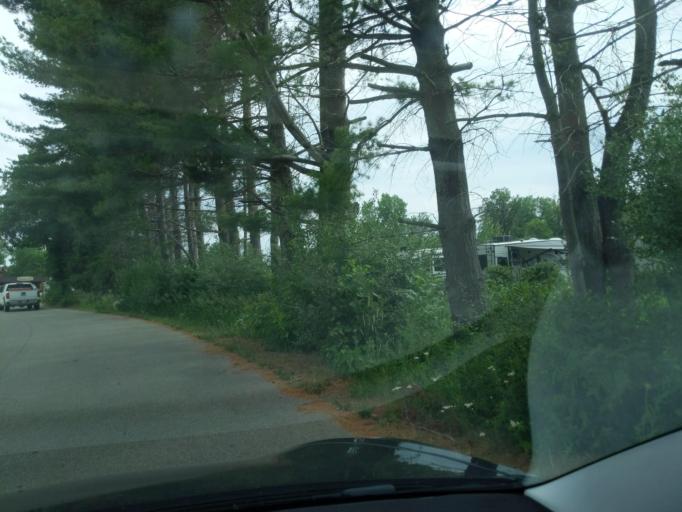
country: US
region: Michigan
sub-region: Isabella County
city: Mount Pleasant
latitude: 43.6181
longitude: -84.7380
